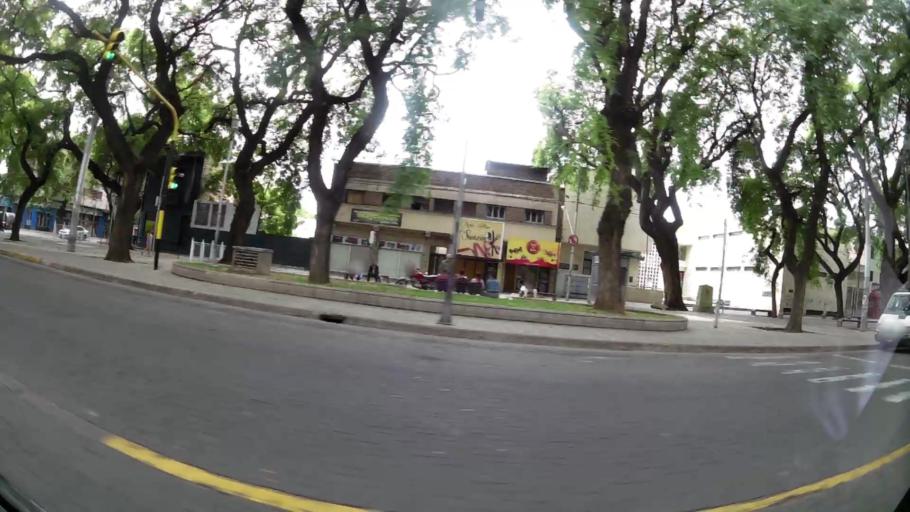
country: AR
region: Mendoza
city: Mendoza
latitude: -32.8813
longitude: -68.8369
